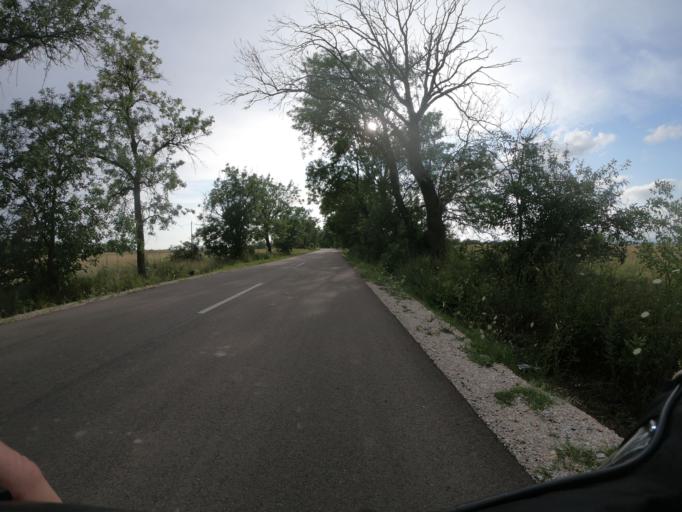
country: HU
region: Borsod-Abauj-Zemplen
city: Mezocsat
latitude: 47.8272
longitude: 20.8203
